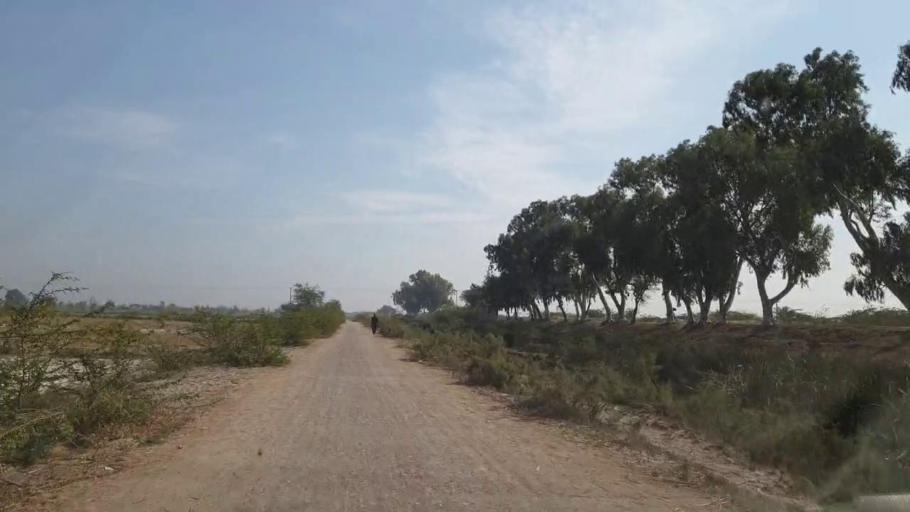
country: PK
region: Sindh
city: Mirpur Khas
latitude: 25.5094
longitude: 69.1227
